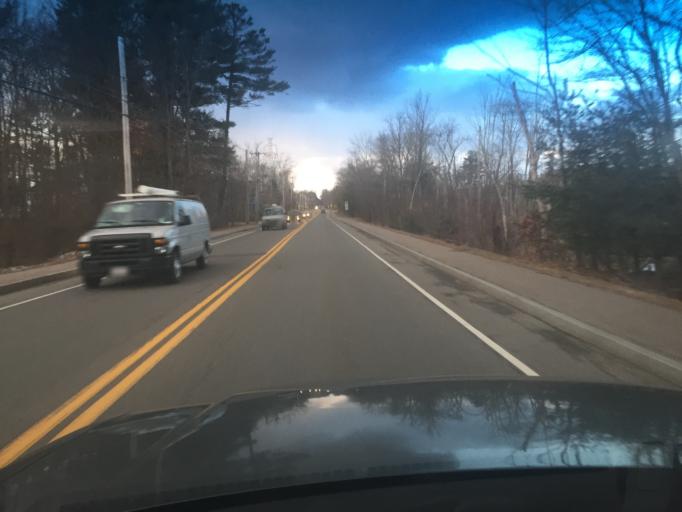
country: US
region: Massachusetts
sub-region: Norfolk County
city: Medway
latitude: 42.1508
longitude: -71.4433
